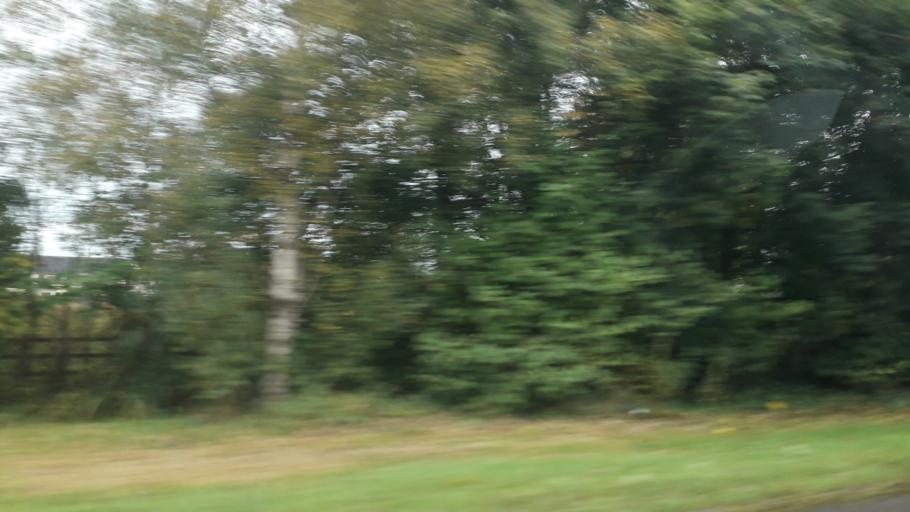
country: IE
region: Leinster
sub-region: An Longfort
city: Longford
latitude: 53.7308
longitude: -7.7720
